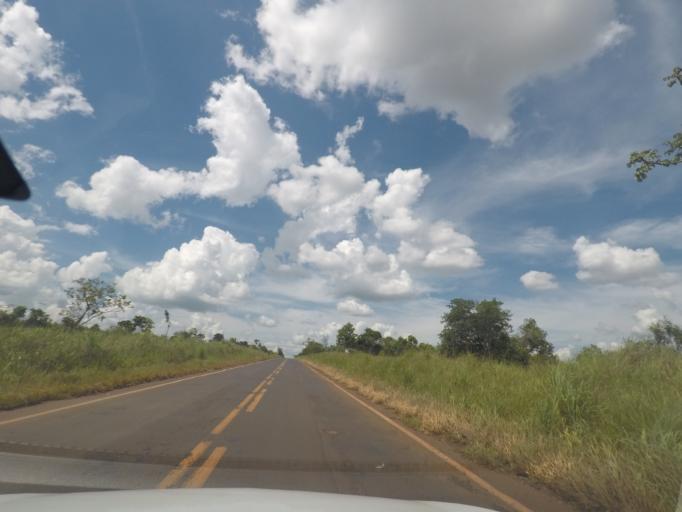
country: BR
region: Minas Gerais
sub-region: Conceicao Das Alagoas
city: Conceicao das Alagoas
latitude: -19.8160
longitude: -48.5883
